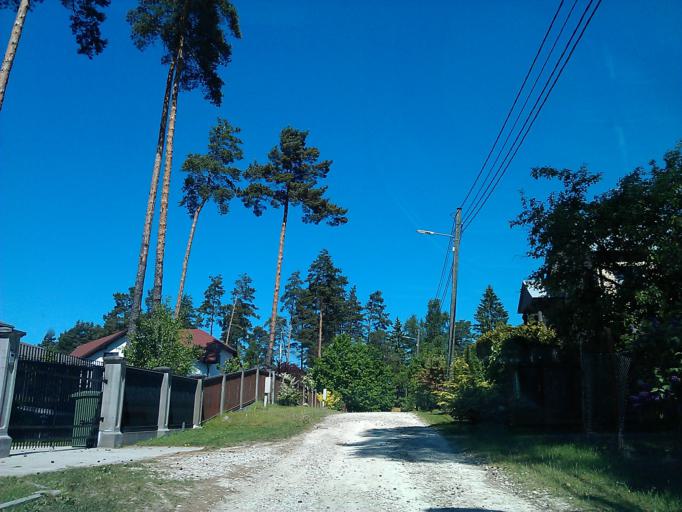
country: LV
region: Riga
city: Bergi
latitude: 57.0053
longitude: 24.3325
